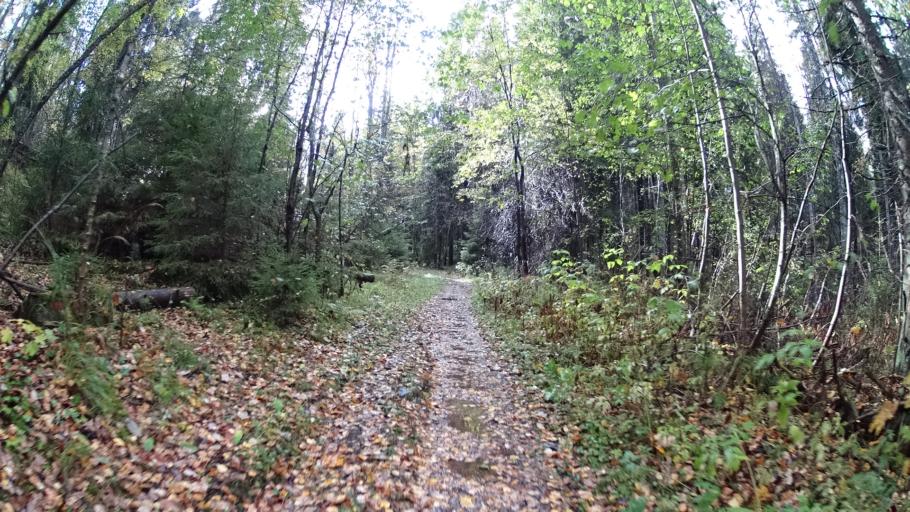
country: FI
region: Uusimaa
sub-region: Helsinki
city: Kilo
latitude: 60.2946
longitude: 24.8029
